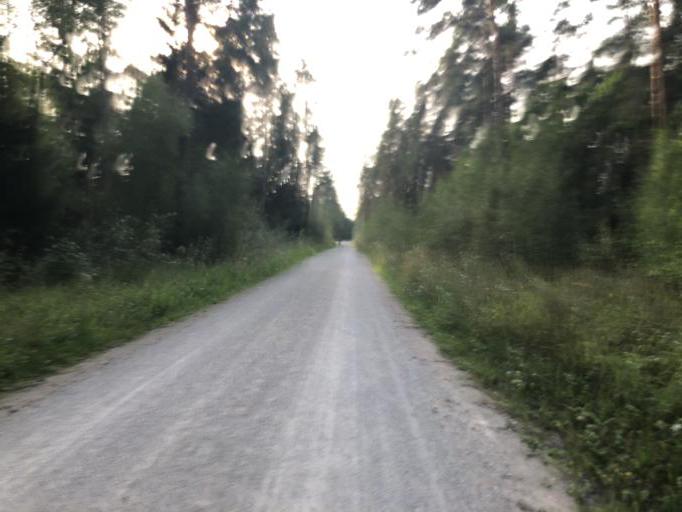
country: DE
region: Bavaria
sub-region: Regierungsbezirk Mittelfranken
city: Buckenhof
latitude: 49.5767
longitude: 11.0495
